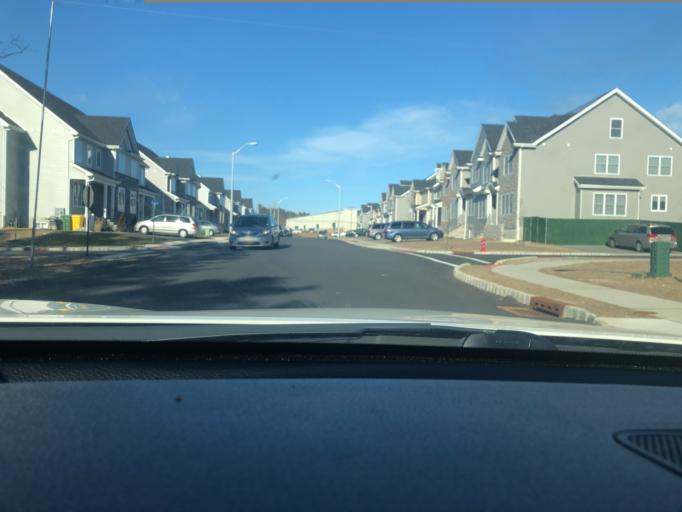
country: US
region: New Jersey
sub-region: Ocean County
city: Lakewood
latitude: 40.0712
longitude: -74.2339
